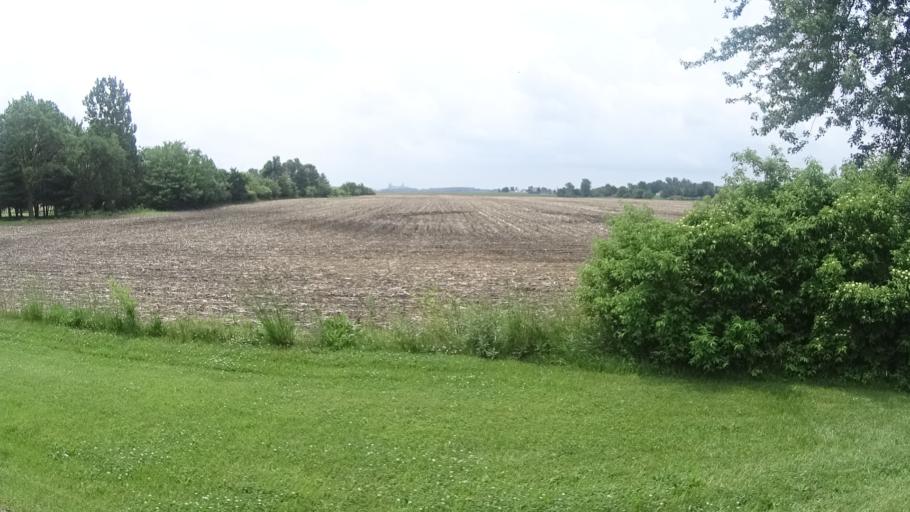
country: US
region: Ohio
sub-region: Huron County
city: Bellevue
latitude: 41.3261
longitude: -82.8263
